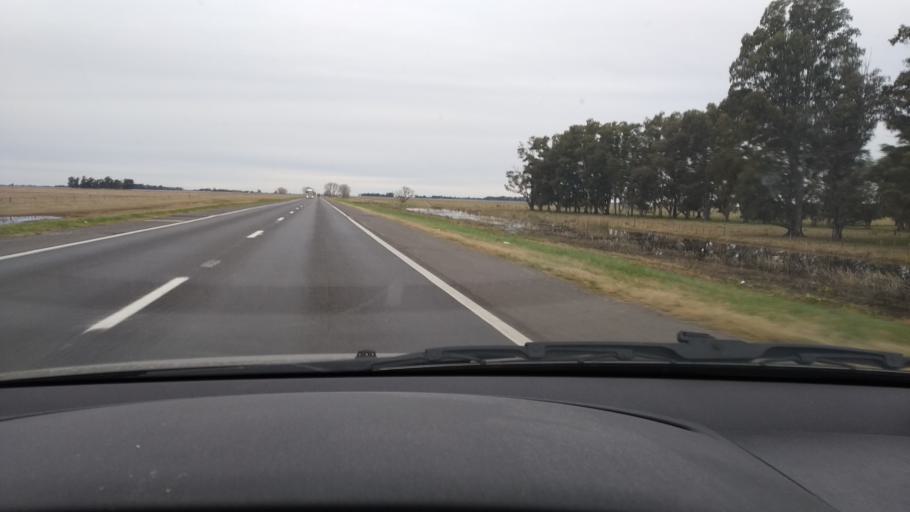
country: AR
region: Buenos Aires
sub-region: Partido de Las Flores
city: Las Flores
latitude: -36.1714
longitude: -59.2394
